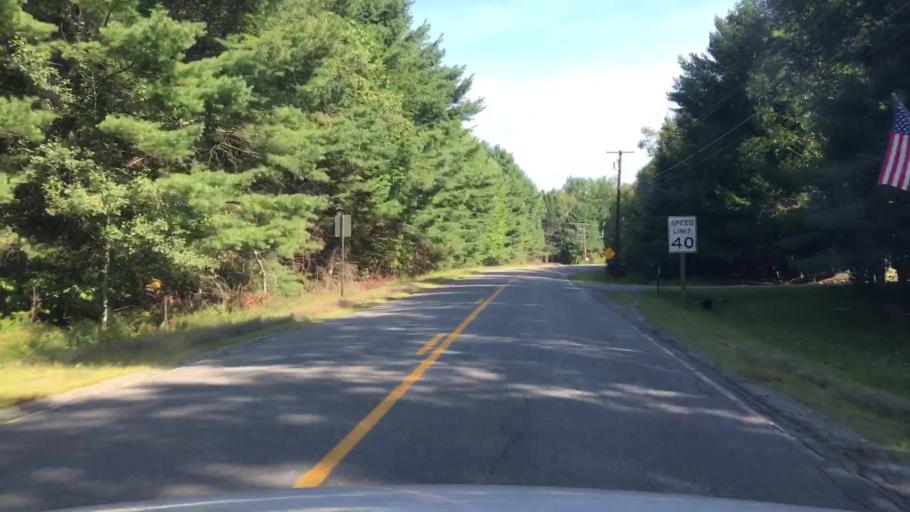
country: US
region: Maine
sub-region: Penobscot County
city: Enfield
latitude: 45.2373
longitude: -68.5474
